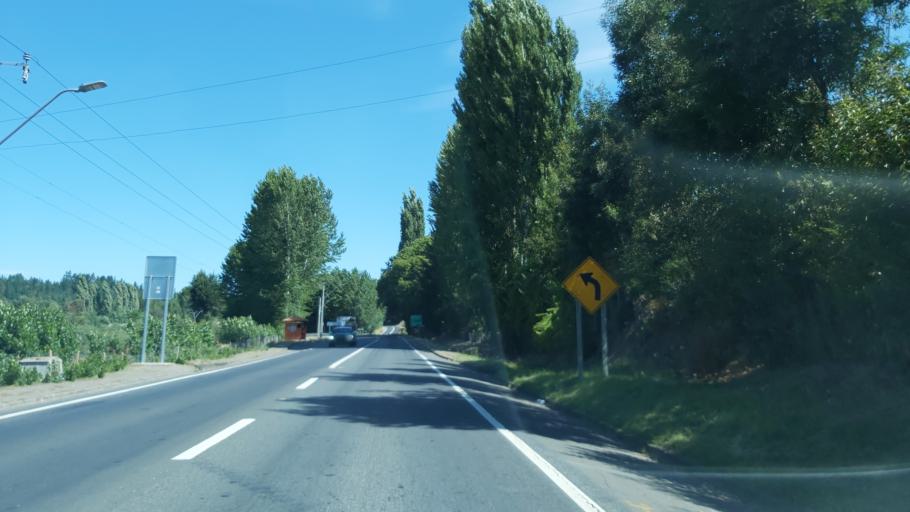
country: CL
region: Biobio
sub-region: Provincia de Concepcion
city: Lota
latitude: -37.1490
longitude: -72.9779
